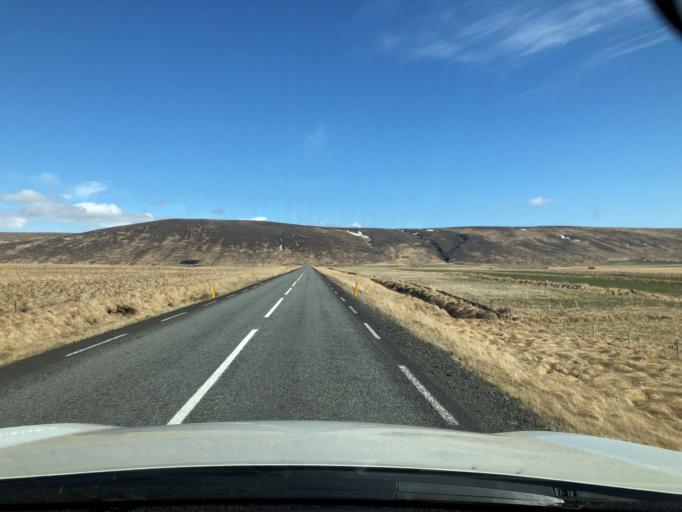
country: IS
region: South
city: Hveragerdi
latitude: 64.6866
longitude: -21.2405
